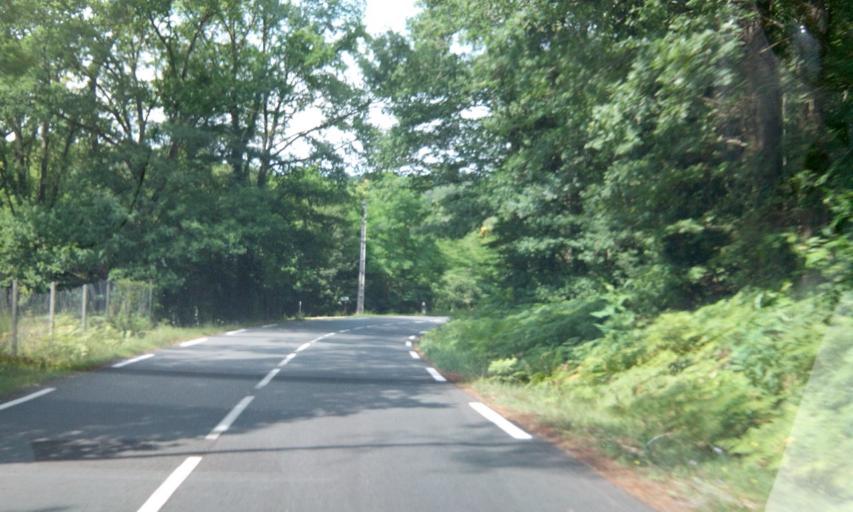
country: FR
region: Aquitaine
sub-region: Departement de la Dordogne
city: Carsac-Aillac
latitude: 44.8653
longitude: 1.2680
